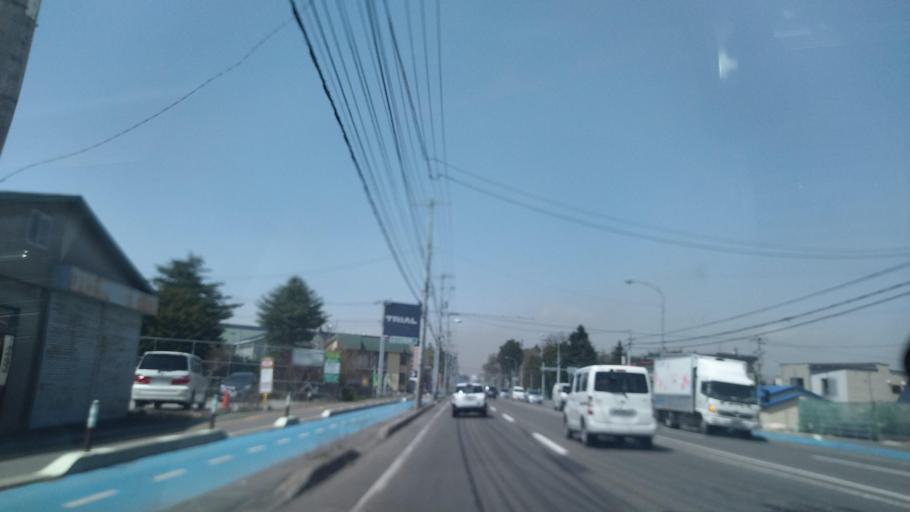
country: JP
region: Hokkaido
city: Obihiro
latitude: 42.9291
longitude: 143.2142
